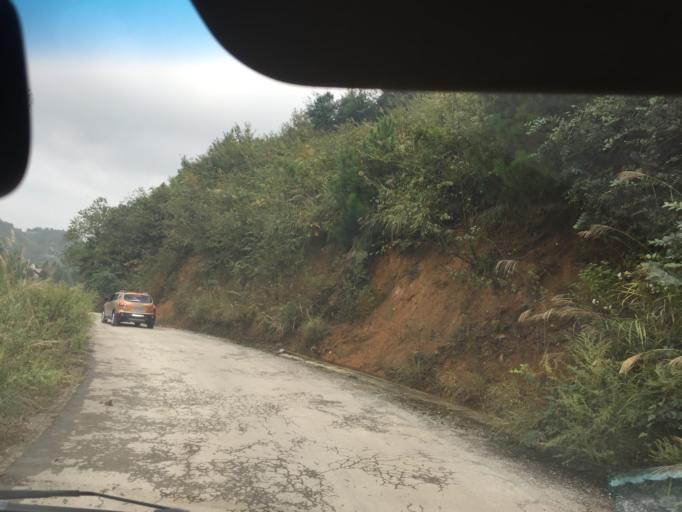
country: CN
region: Guizhou Sheng
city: Guiyang
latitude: 26.8993
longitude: 107.1984
